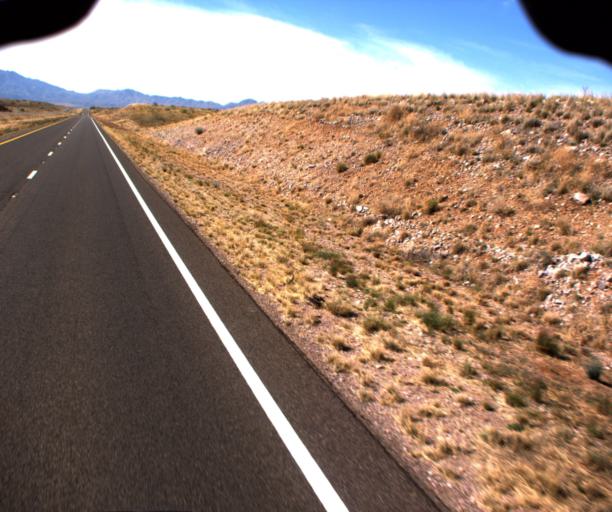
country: US
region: Arizona
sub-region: Cochise County
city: Willcox
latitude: 32.4260
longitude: -109.6632
